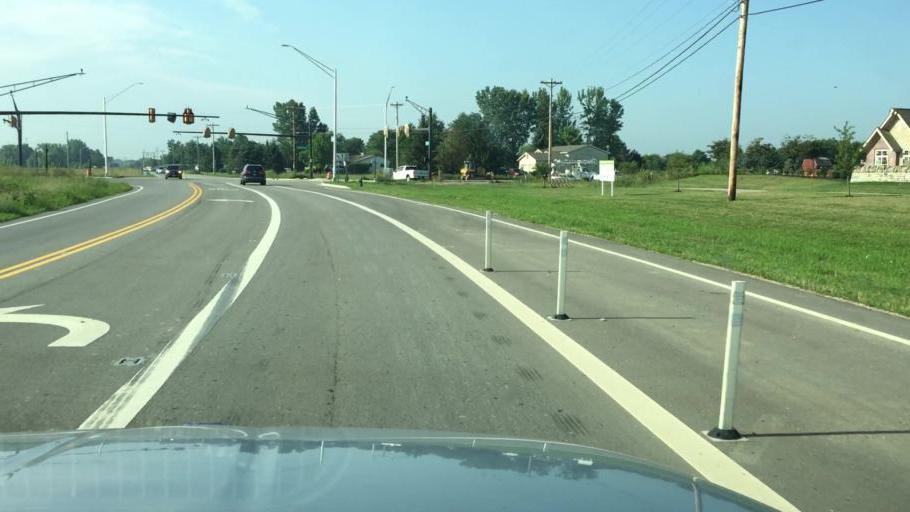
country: US
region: Ohio
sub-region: Franklin County
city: Hilliard
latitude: 40.0644
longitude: -83.1609
